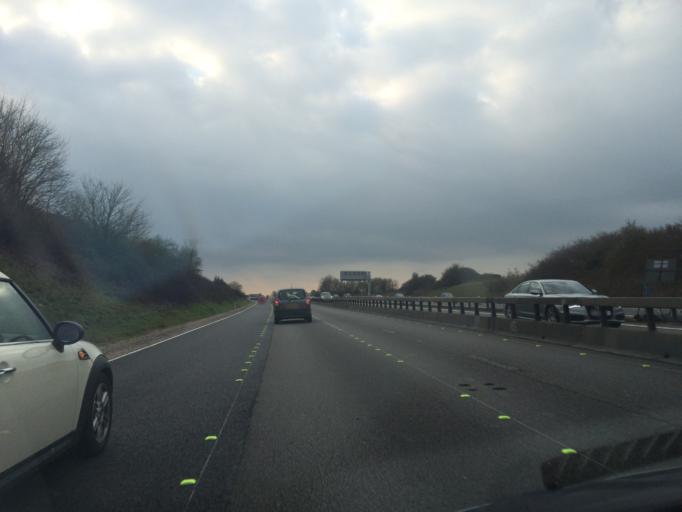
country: GB
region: England
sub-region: West Berkshire
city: Winterbourne
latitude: 51.4554
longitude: -1.3437
